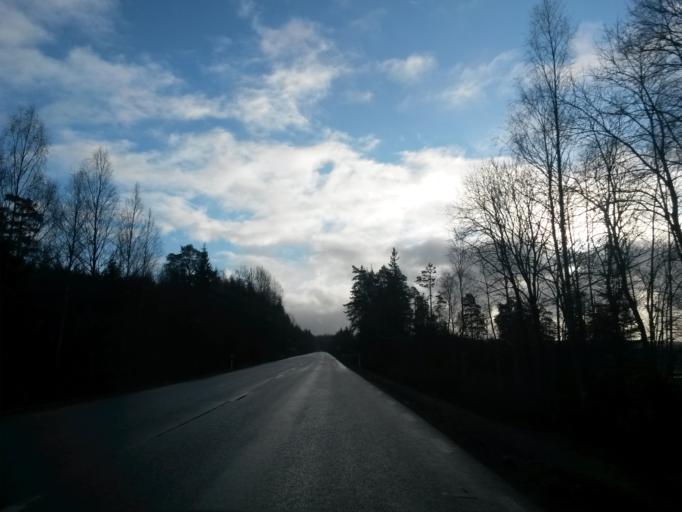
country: SE
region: Vaestra Goetaland
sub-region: Boras Kommun
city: Boras
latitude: 57.8579
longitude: 12.9431
